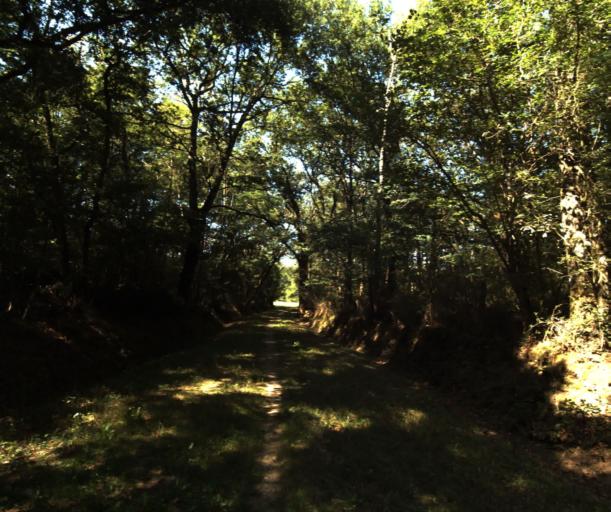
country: FR
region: Midi-Pyrenees
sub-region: Departement de la Haute-Garonne
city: Fonsorbes
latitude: 43.5178
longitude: 1.2139
